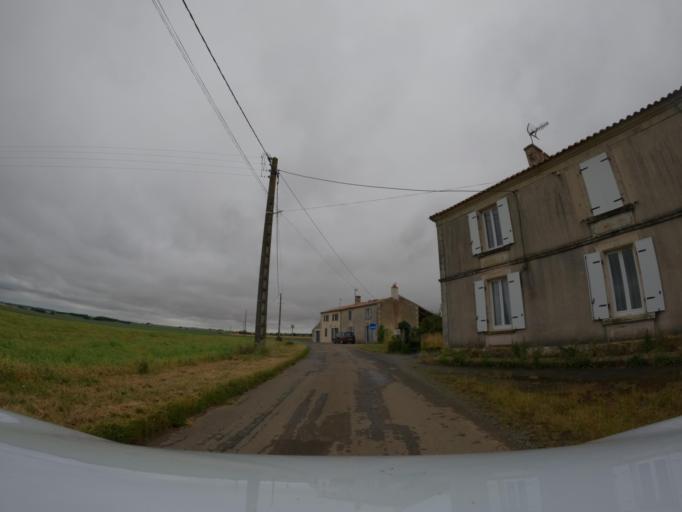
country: FR
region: Pays de la Loire
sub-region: Departement de la Vendee
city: Maillezais
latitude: 46.4186
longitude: -0.7184
